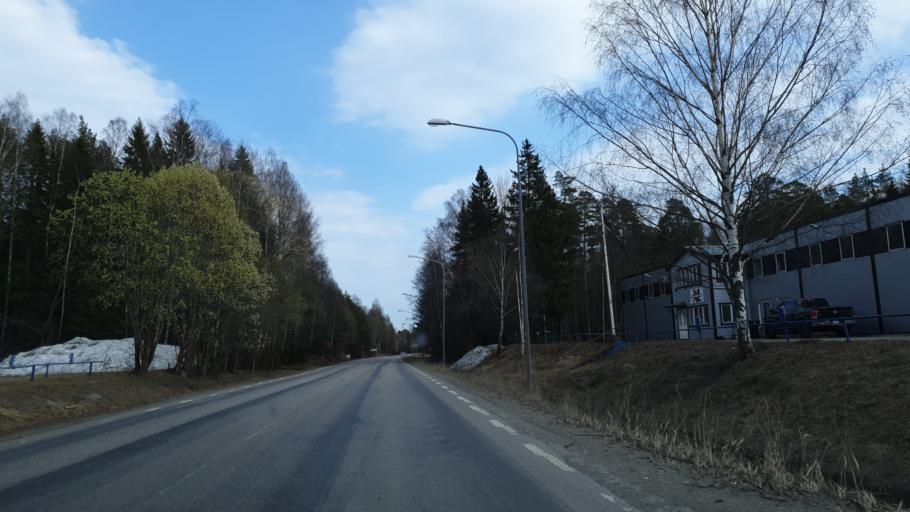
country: SE
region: Gaevleborg
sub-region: Hudiksvalls Kommun
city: Iggesund
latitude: 61.6436
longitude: 17.0599
